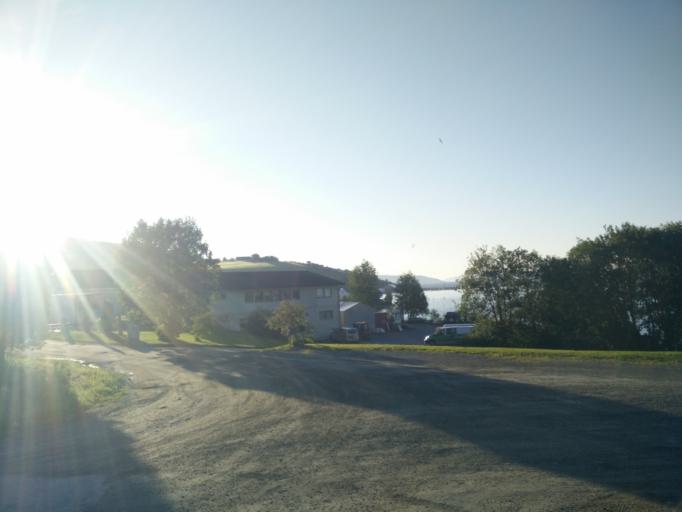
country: NO
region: Sor-Trondelag
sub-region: Skaun
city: Borsa
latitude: 63.3240
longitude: 10.0785
